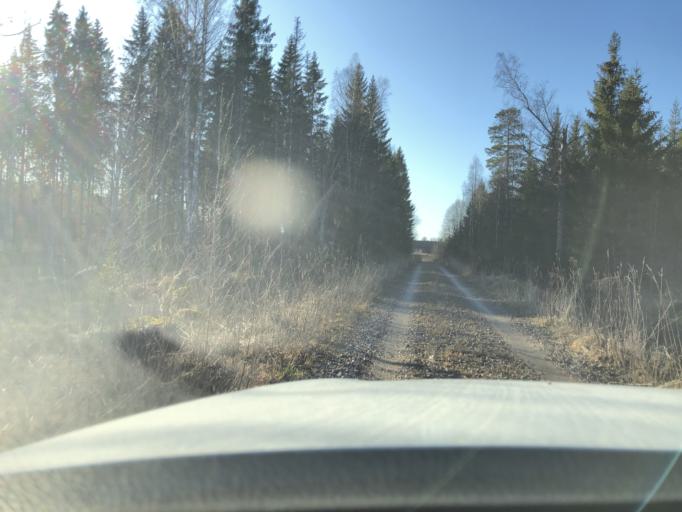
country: SE
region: Gaevleborg
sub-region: Gavle Kommun
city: Hedesunda
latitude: 60.2985
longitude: 16.8886
